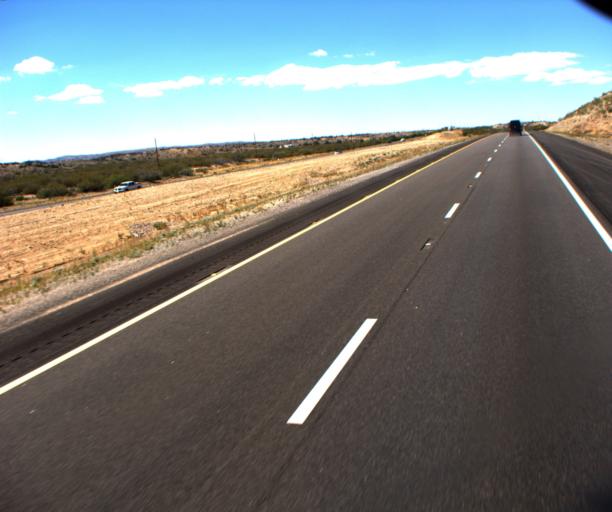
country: US
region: Arizona
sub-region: Mohave County
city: Kingman
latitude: 35.0179
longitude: -113.6640
